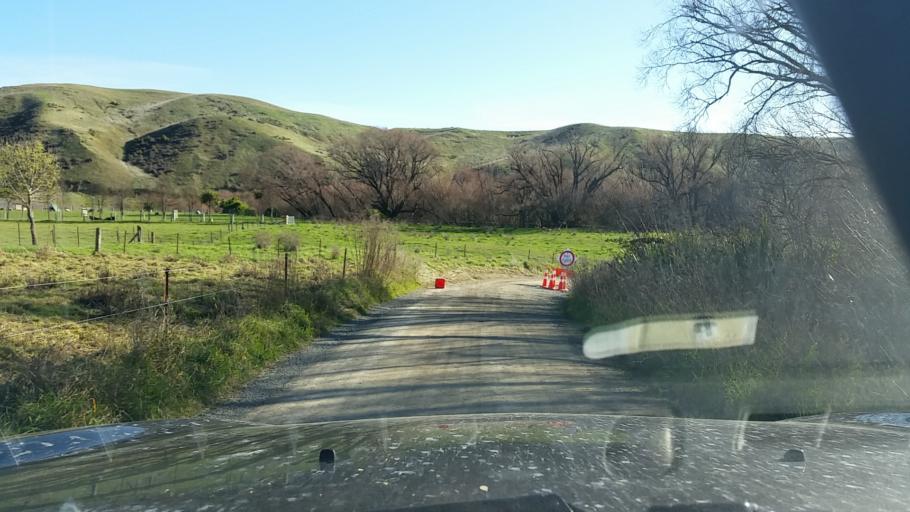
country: NZ
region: Marlborough
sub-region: Marlborough District
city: Blenheim
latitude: -41.6796
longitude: 174.1343
